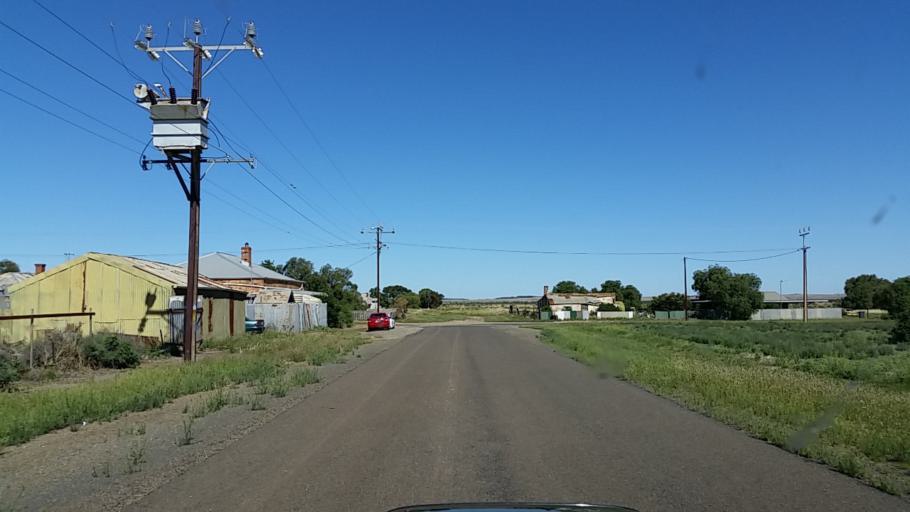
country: AU
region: South Australia
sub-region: Peterborough
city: Peterborough
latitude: -33.1524
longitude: 138.9170
